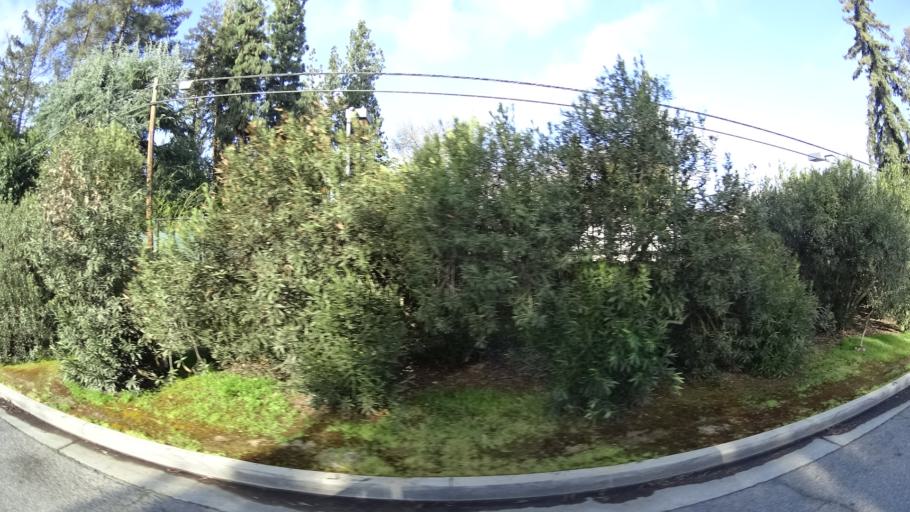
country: US
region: California
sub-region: Fresno County
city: Fresno
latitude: 36.8173
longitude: -119.8309
